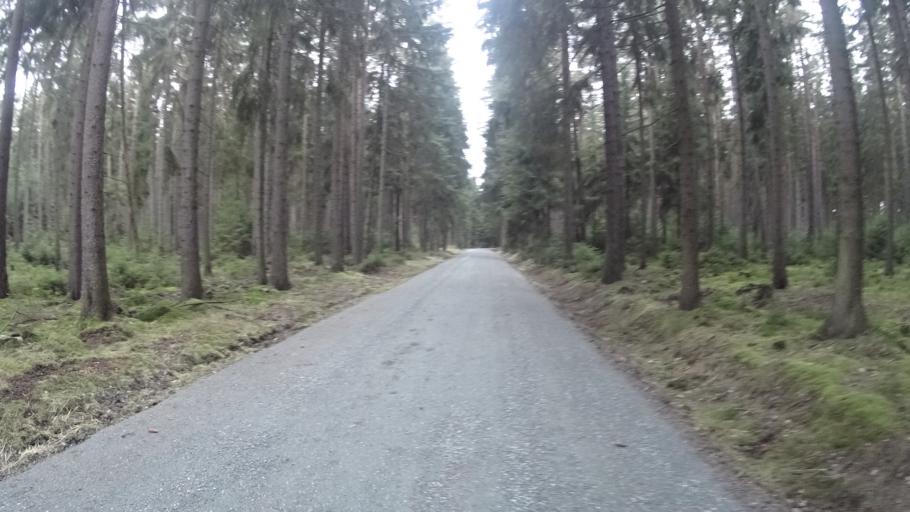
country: DE
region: Saxony
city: Pausa
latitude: 50.6105
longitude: 11.9996
